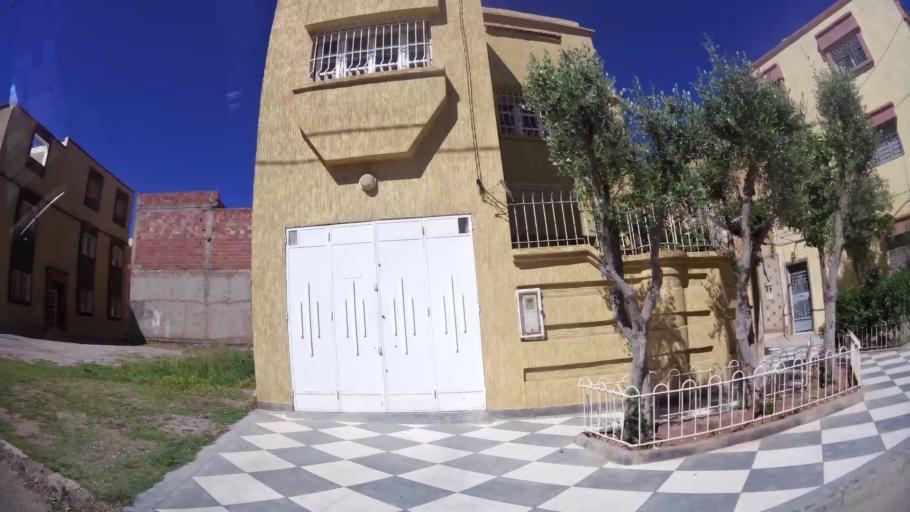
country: MA
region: Oriental
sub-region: Oujda-Angad
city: Oujda
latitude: 34.6596
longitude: -1.8889
